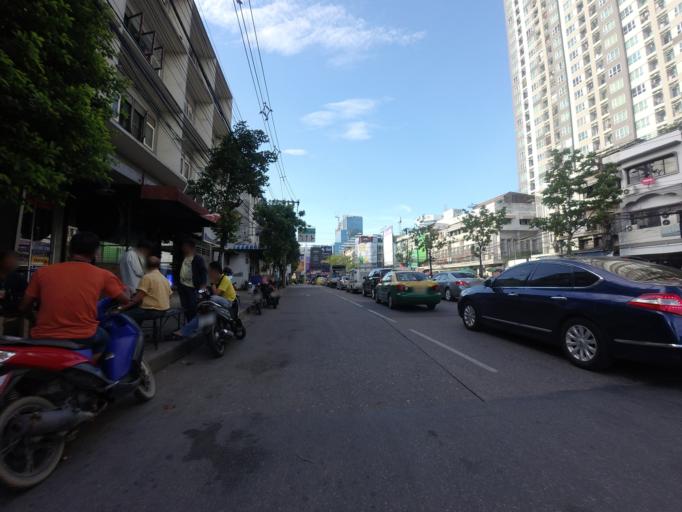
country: TH
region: Bangkok
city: Khlong Toei
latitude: 13.7121
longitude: 100.5838
